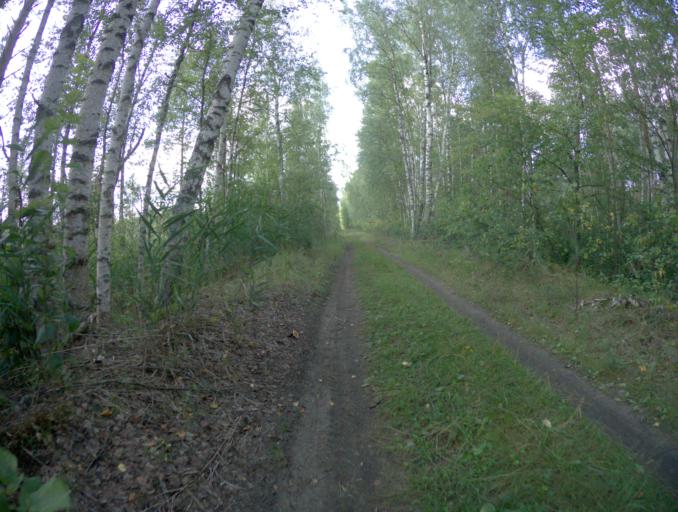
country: RU
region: Vladimir
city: Sobinka
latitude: 55.9366
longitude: 40.0602
